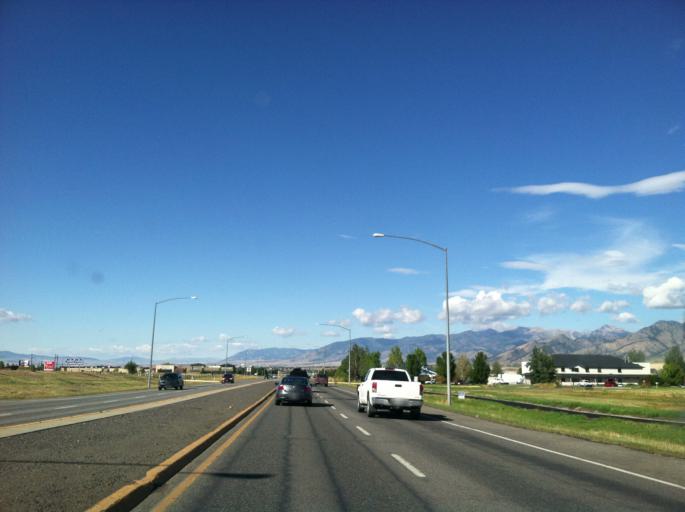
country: US
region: Montana
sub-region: Gallatin County
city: Bozeman
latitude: 45.7033
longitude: -111.0656
